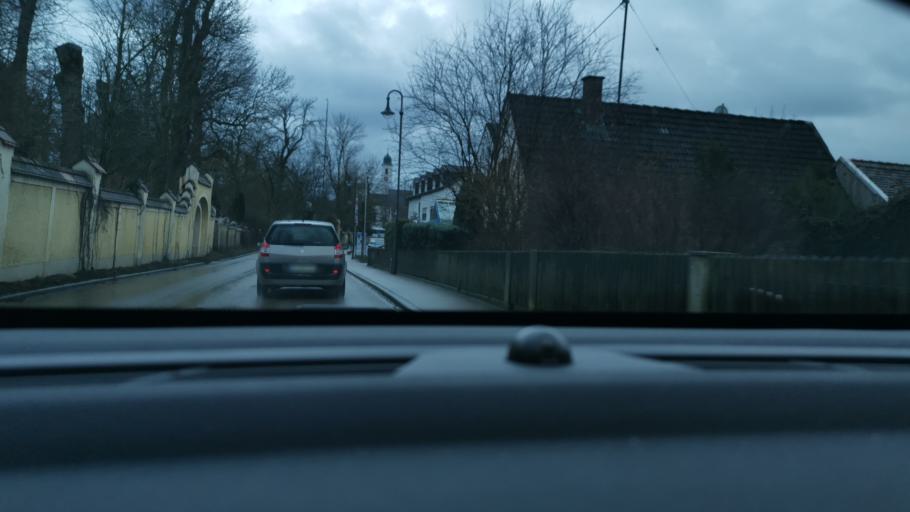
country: DE
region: Bavaria
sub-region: Swabia
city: Affing
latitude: 48.4610
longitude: 10.9814
